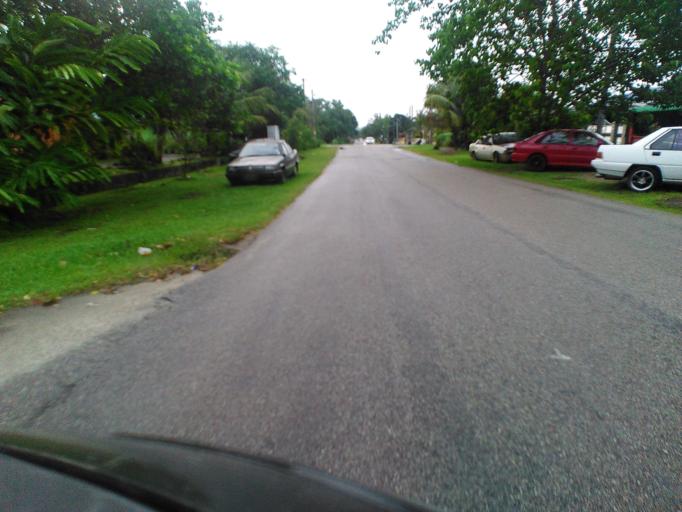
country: MY
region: Kedah
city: Kulim
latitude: 5.3665
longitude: 100.5675
